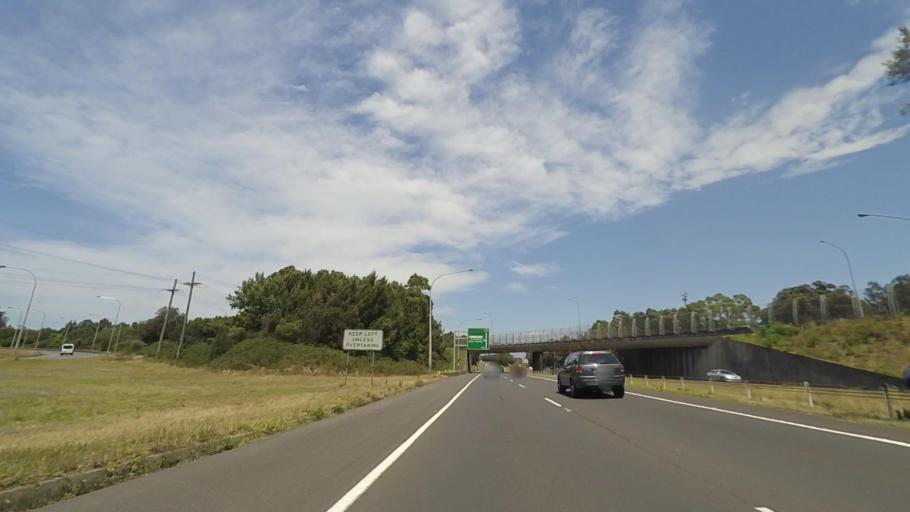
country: AU
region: New South Wales
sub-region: Wollongong
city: Mangerton
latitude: -34.4403
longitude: 150.8652
